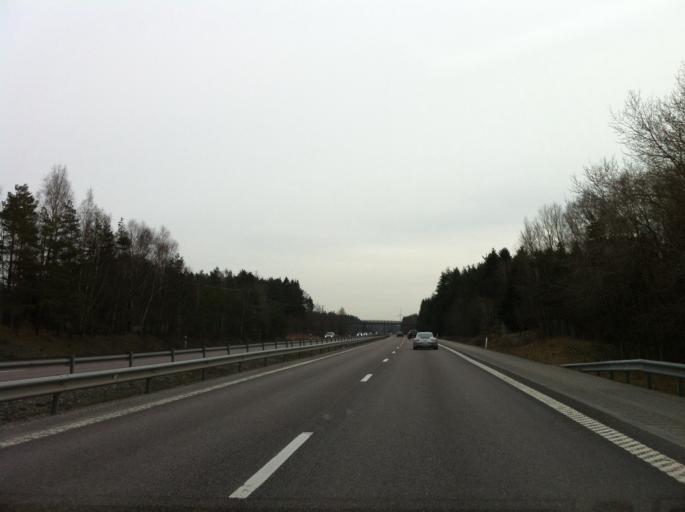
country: SE
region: Vaestra Goetaland
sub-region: Stenungsunds Kommun
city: Stora Hoga
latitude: 57.9928
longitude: 11.8421
